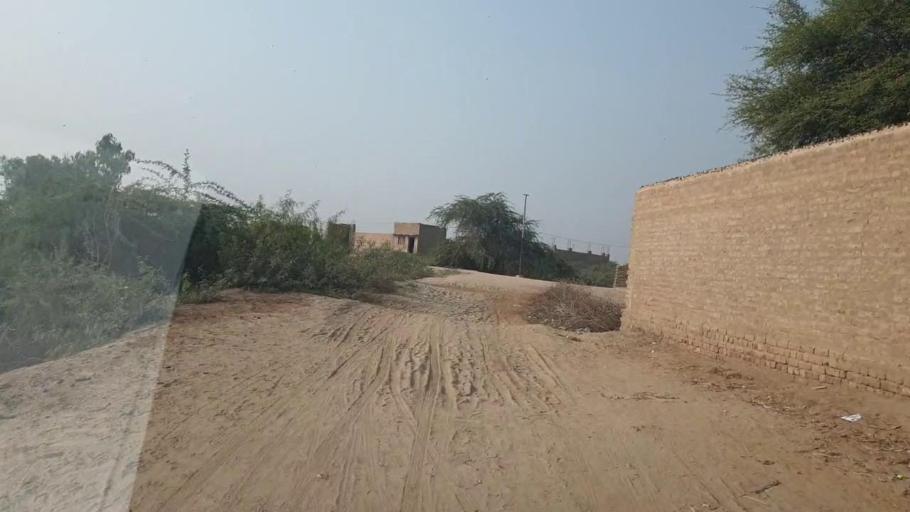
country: PK
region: Sindh
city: Tando Jam
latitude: 25.3337
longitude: 68.5269
